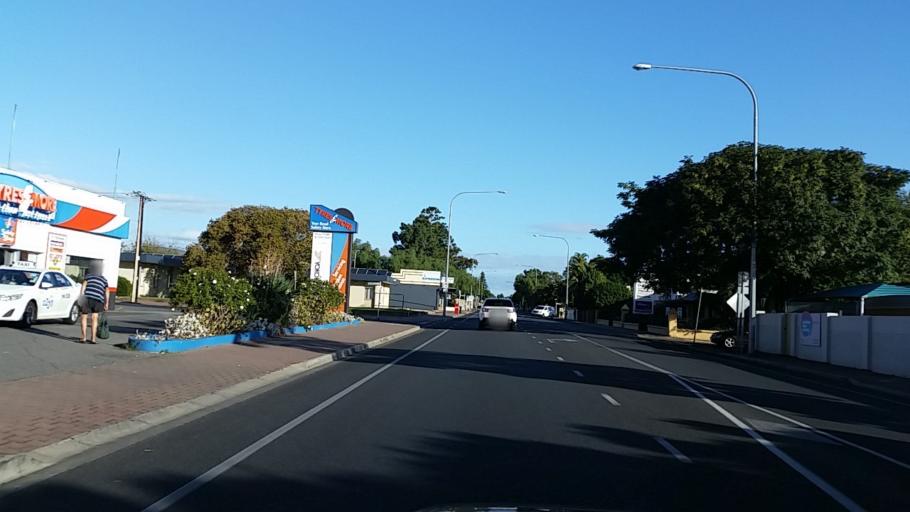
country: AU
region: South Australia
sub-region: Prospect
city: Prospect
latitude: -34.8929
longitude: 138.5945
